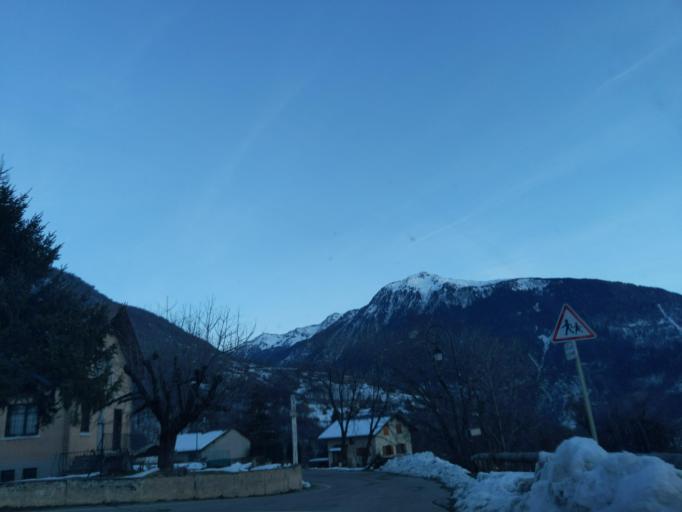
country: FR
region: Rhone-Alpes
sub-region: Departement de la Savoie
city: Saint-Michel-de-Maurienne
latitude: 45.2304
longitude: 6.4636
